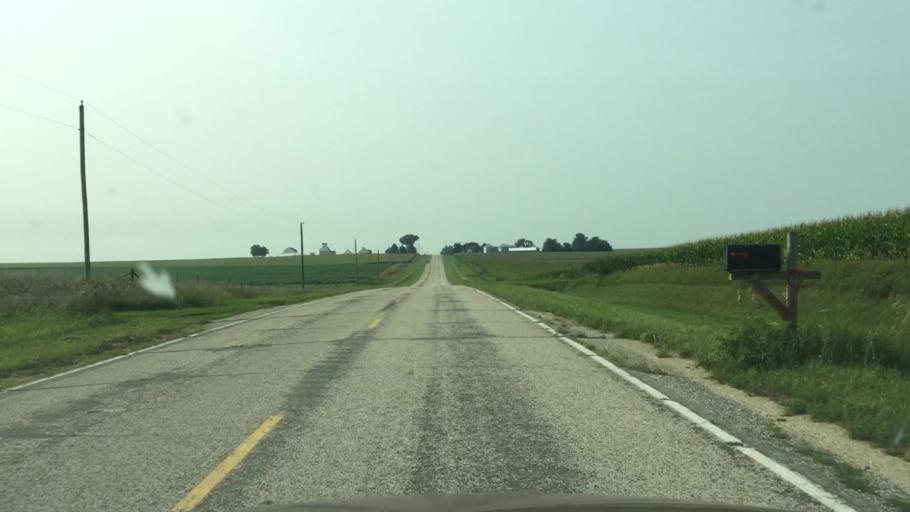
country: US
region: Iowa
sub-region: O'Brien County
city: Sheldon
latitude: 43.2769
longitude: -95.7829
